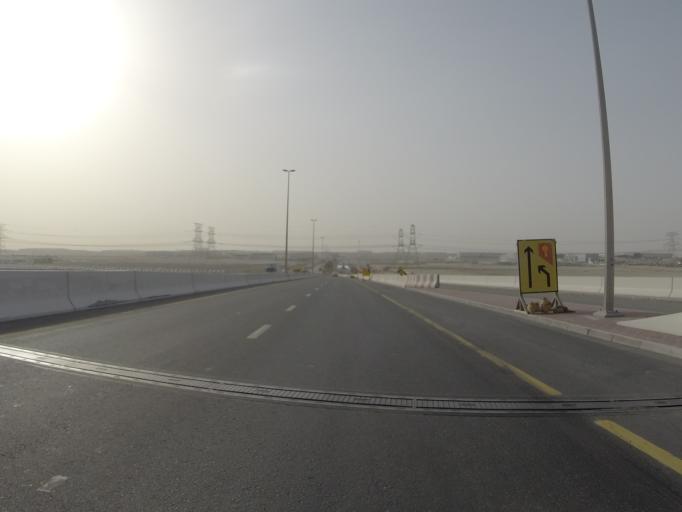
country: AE
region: Dubai
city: Dubai
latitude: 24.9576
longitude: 55.1007
